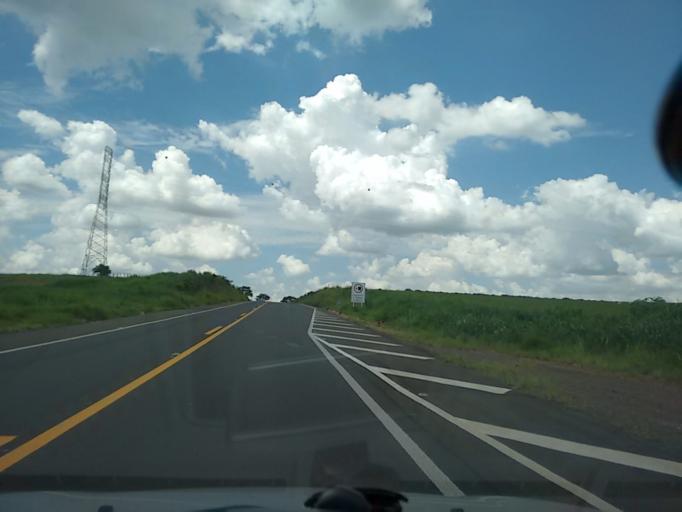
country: BR
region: Sao Paulo
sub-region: Osvaldo Cruz
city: Osvaldo Cruz
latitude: -21.8690
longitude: -50.8535
